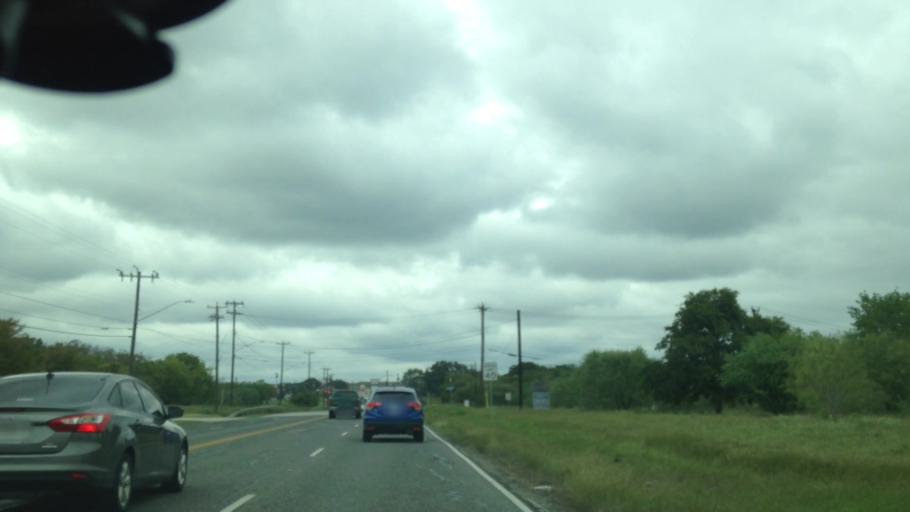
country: US
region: Texas
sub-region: Bexar County
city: Windcrest
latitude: 29.5580
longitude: -98.3824
